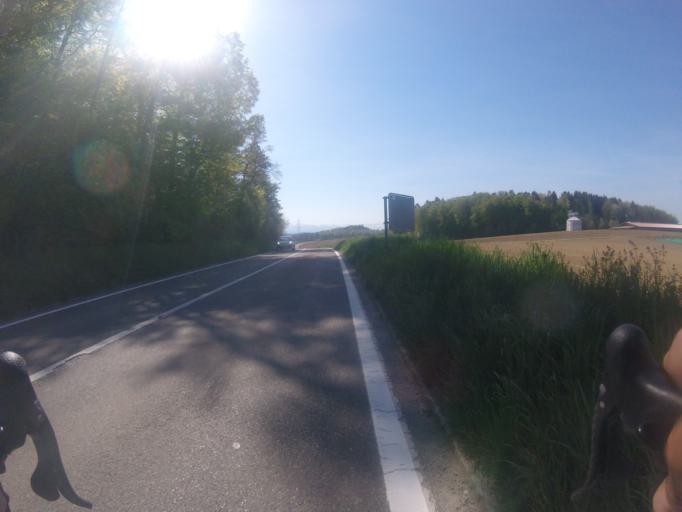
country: CH
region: Bern
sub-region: Bern-Mittelland District
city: Ferenbalm
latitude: 46.9496
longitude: 7.2277
